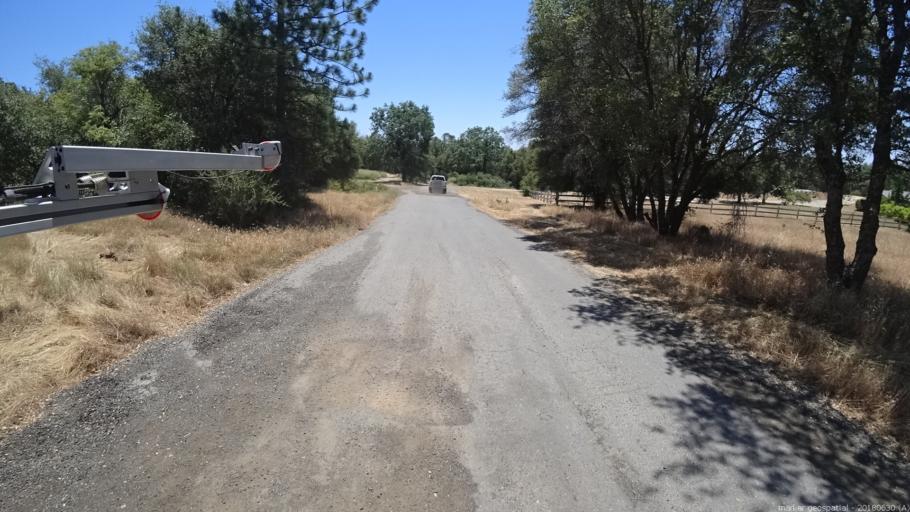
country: US
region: California
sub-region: Fresno County
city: Auberry
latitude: 37.2184
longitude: -119.4894
